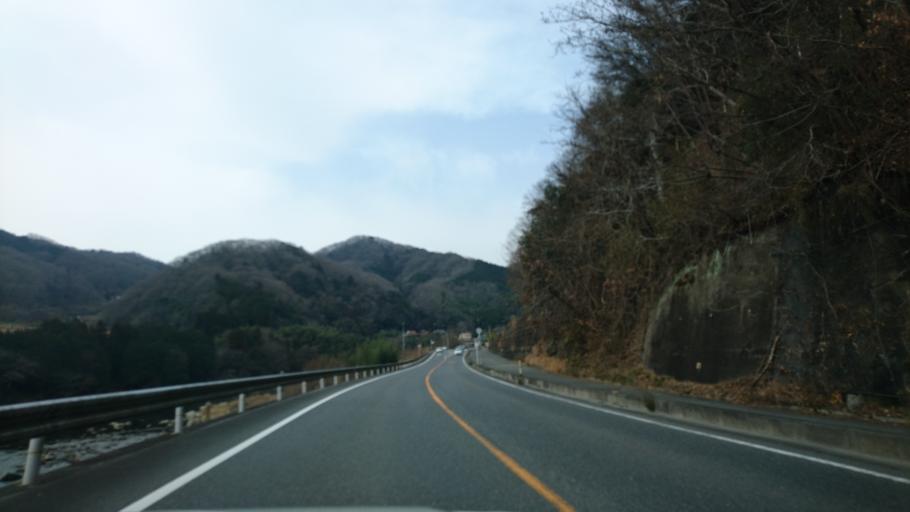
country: JP
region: Okayama
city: Takahashi
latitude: 34.8375
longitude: 133.5981
